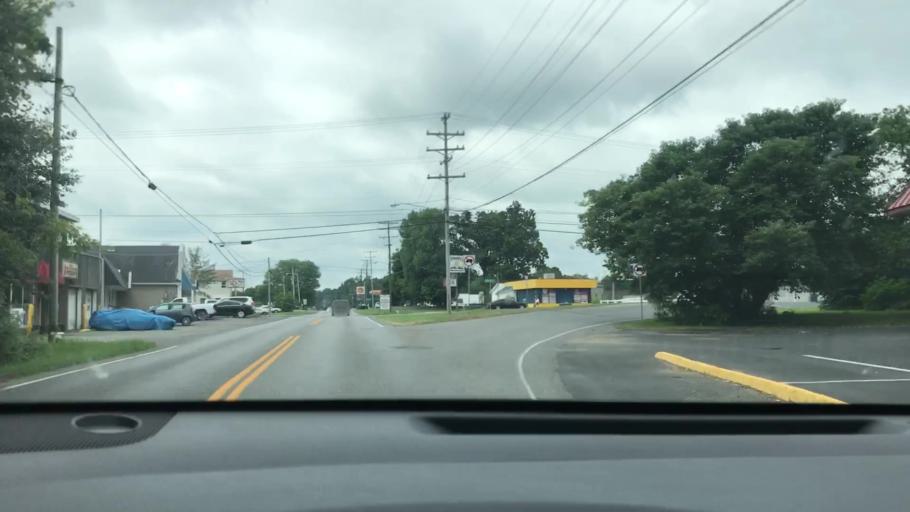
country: US
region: Kentucky
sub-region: Calloway County
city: Murray
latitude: 36.6033
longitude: -88.3025
